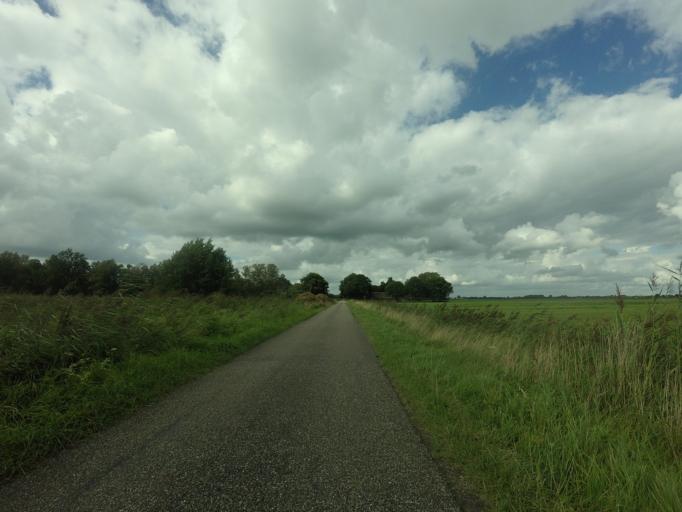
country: NL
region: Overijssel
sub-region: Gemeente Steenwijkerland
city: Giethoorn
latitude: 52.7229
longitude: 6.0512
